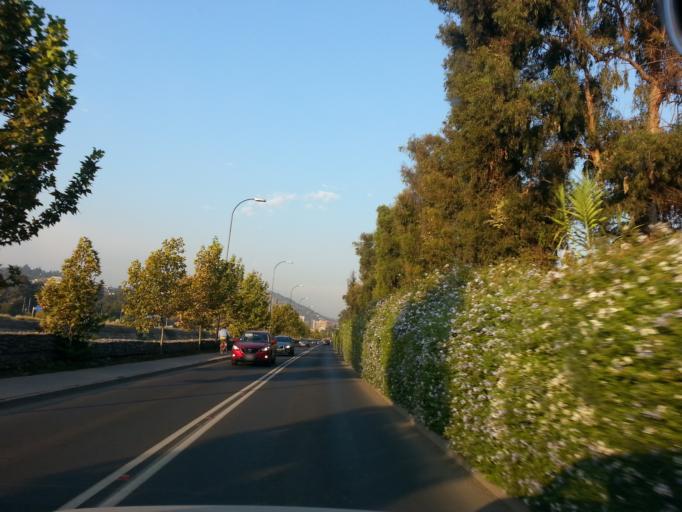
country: CL
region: Santiago Metropolitan
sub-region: Provincia de Santiago
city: Villa Presidente Frei, Nunoa, Santiago, Chile
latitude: -33.3778
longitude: -70.5645
